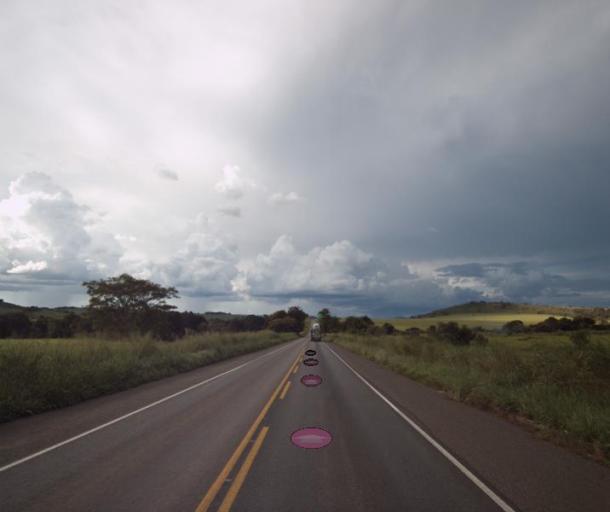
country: BR
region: Goias
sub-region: Ceres
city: Ceres
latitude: -15.2359
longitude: -49.5558
